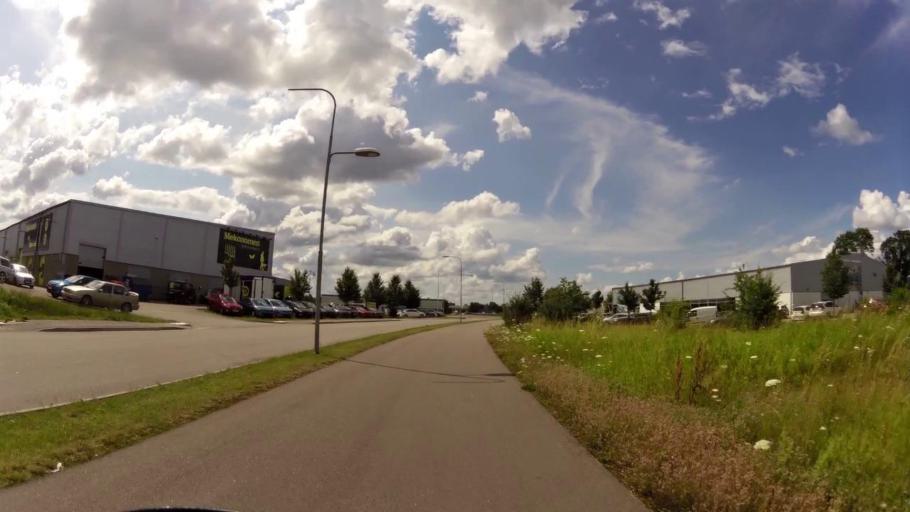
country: SE
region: OEstergoetland
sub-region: Linkopings Kommun
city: Linkoping
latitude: 58.4311
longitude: 15.6012
